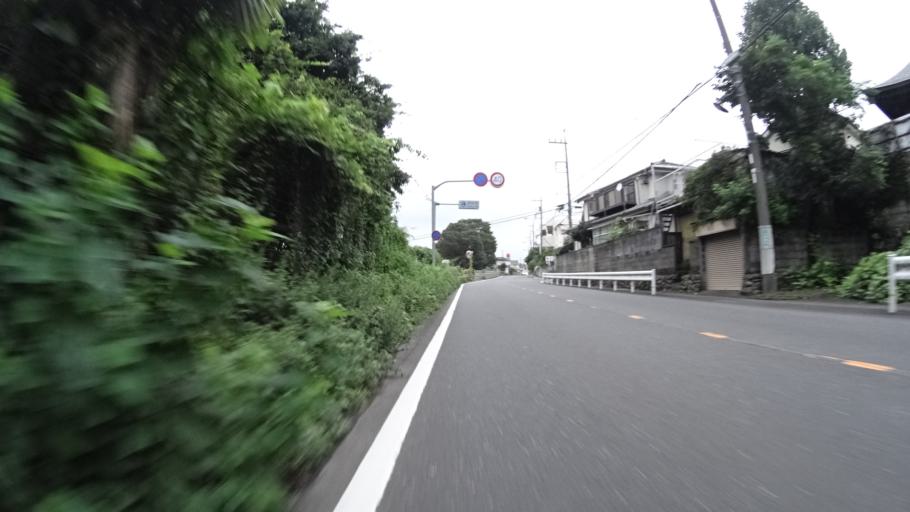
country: JP
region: Tokyo
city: Fussa
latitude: 35.7486
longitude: 139.3176
